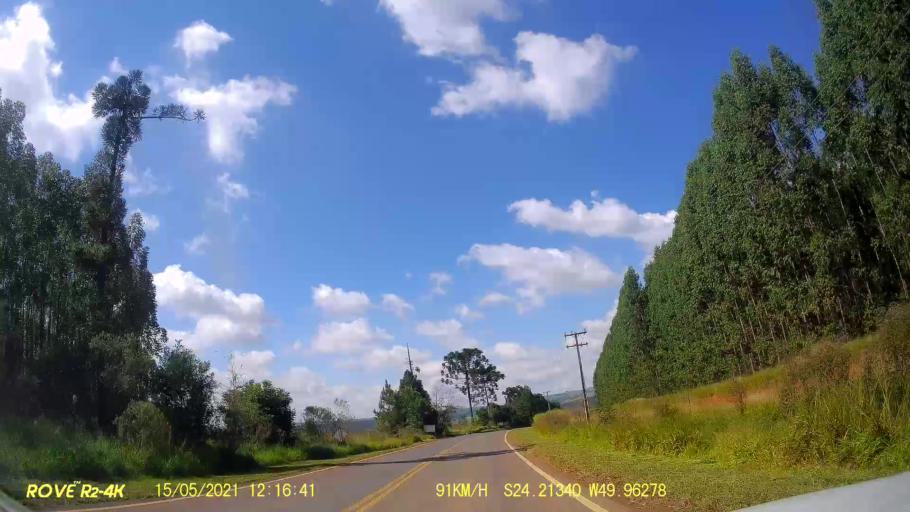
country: BR
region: Parana
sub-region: Jaguariaiva
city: Jaguariaiva
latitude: -24.2134
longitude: -49.9627
